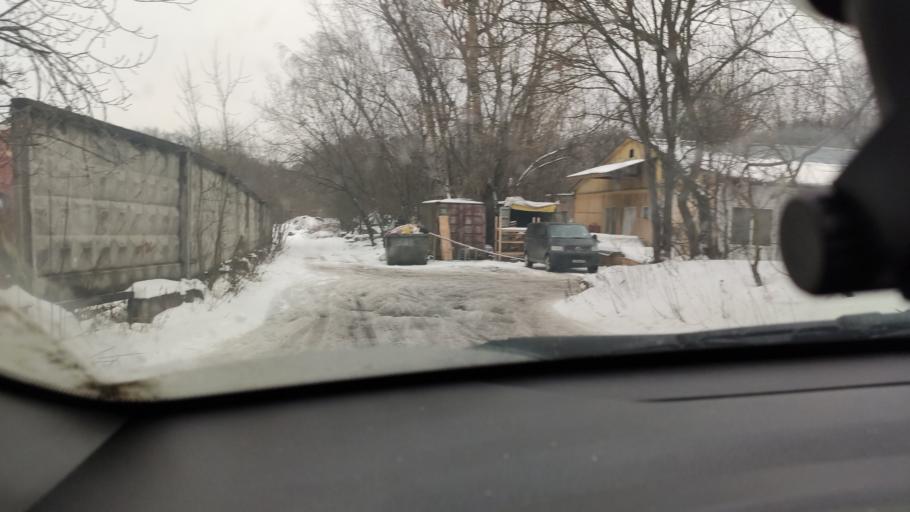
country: RU
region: Moscow
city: Chertanovo Yuzhnoye
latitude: 55.5928
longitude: 37.5805
